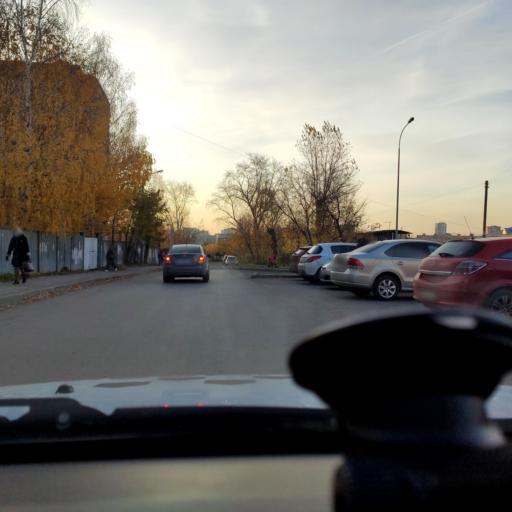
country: RU
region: Perm
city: Perm
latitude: 57.9745
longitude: 56.2123
